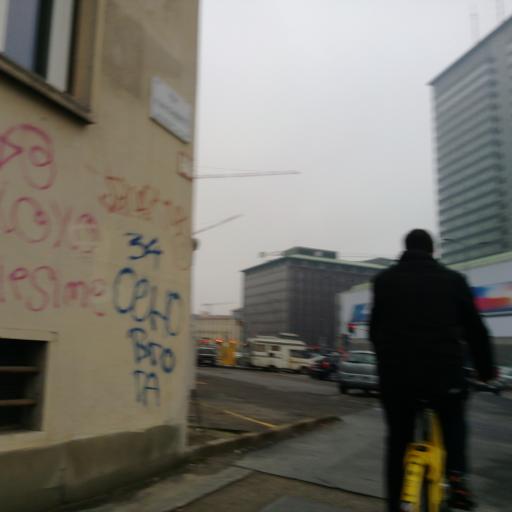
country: IT
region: Lombardy
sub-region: Citta metropolitana di Milano
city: Milano
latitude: 45.4854
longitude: 9.1946
